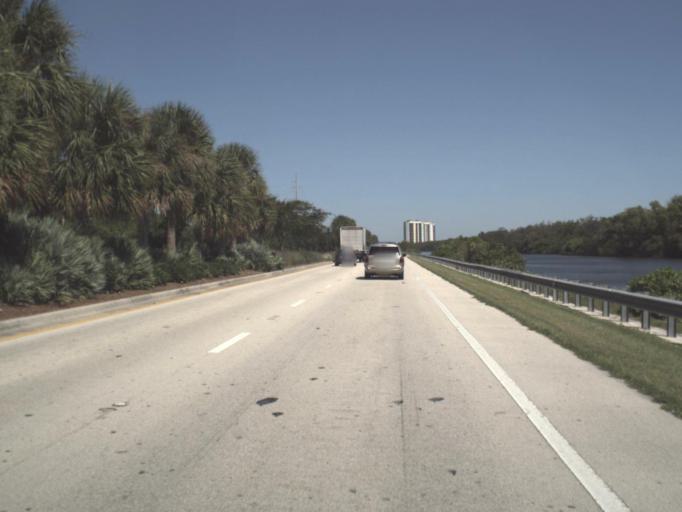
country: US
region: Florida
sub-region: Collier County
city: Marco
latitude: 25.9726
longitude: -81.7067
